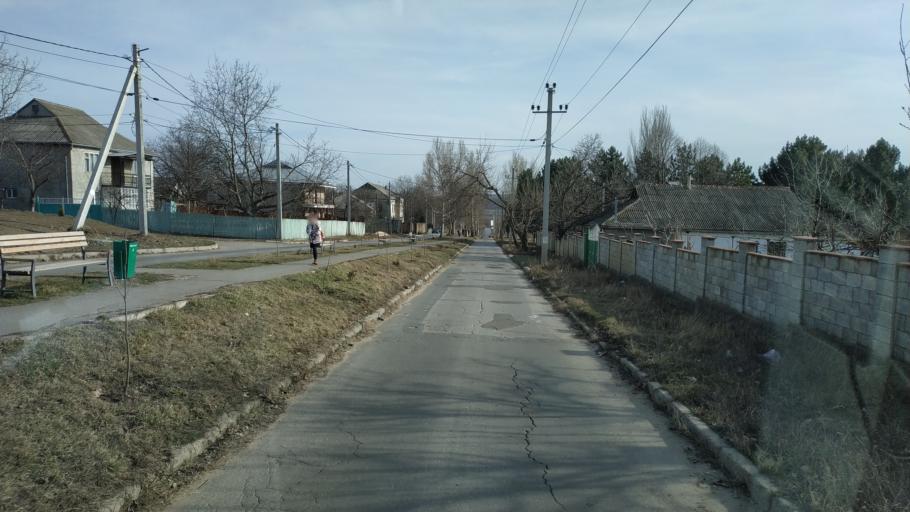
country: MD
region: Chisinau
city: Vatra
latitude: 47.0744
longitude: 28.6929
